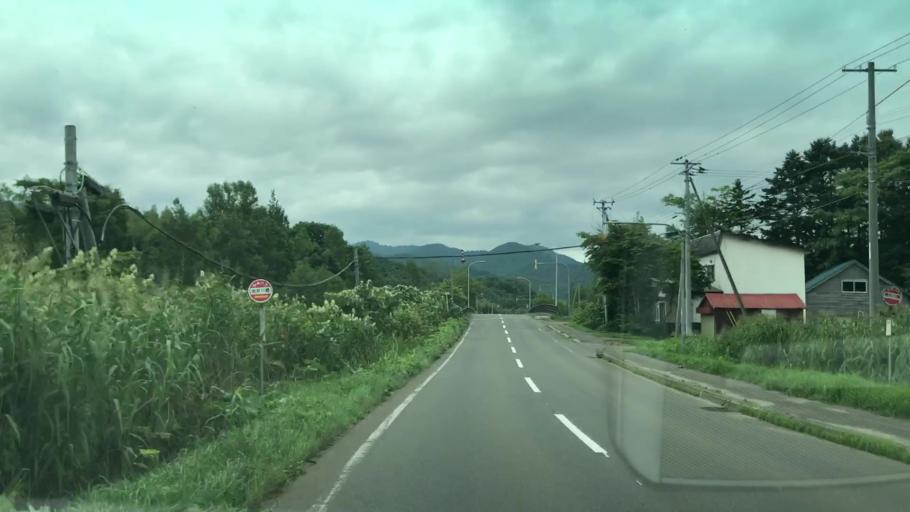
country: JP
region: Hokkaido
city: Yoichi
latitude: 43.0606
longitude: 140.8214
